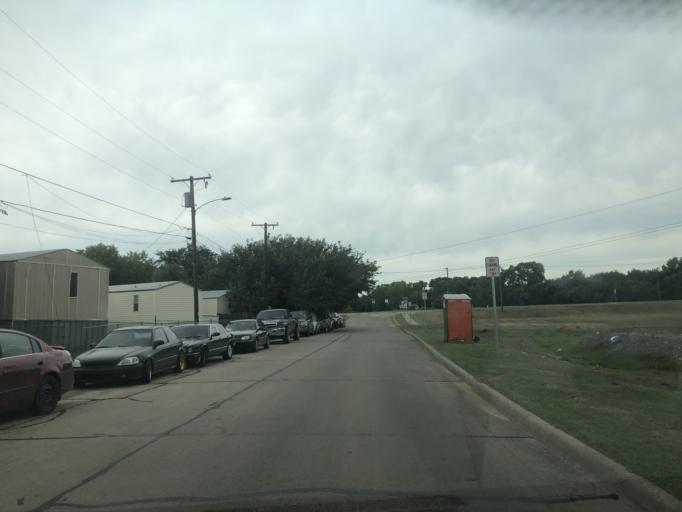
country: US
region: Texas
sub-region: Dallas County
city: Irving
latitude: 32.7843
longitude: -96.9734
